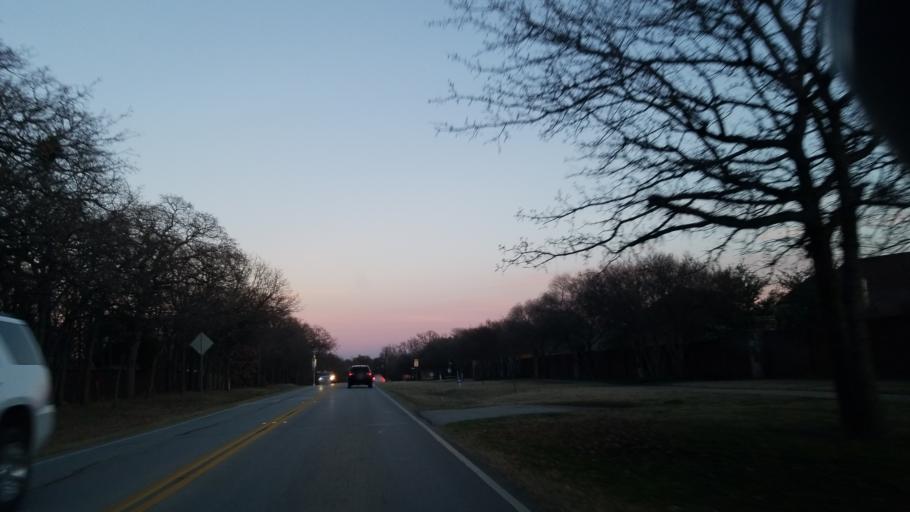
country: US
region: Texas
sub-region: Denton County
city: Denton
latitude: 33.1615
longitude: -97.1300
